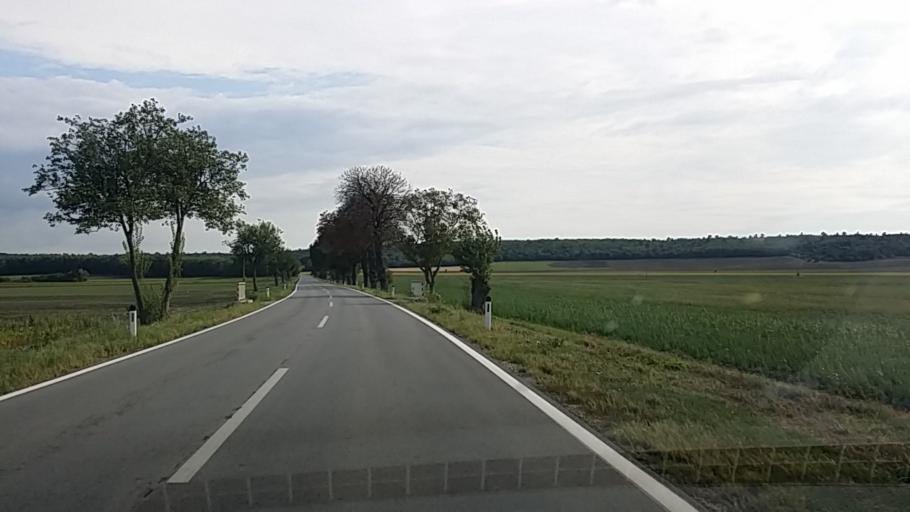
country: AT
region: Burgenland
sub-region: Eisenstadt-Umgebung
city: Sankt Margarethen im Burgenland
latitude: 47.7798
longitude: 16.6164
